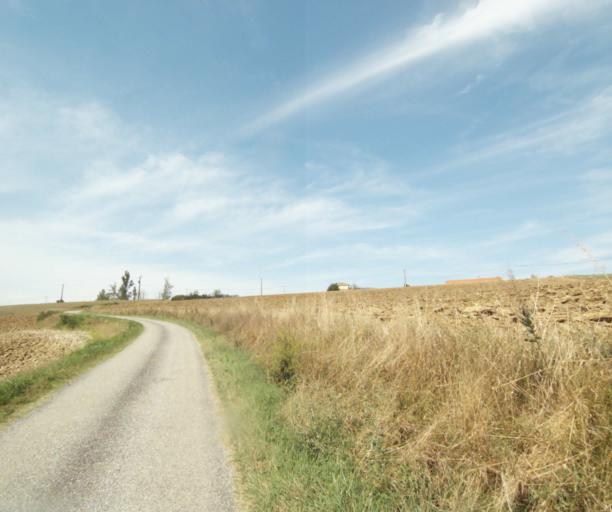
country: FR
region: Midi-Pyrenees
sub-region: Departement de la Haute-Garonne
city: Gaillac-Toulza
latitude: 43.2635
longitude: 1.4103
